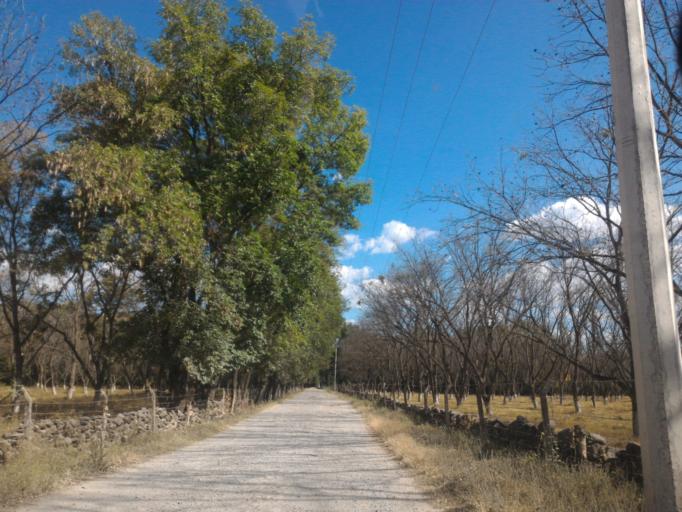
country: MX
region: Jalisco
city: San Diego de Alejandria
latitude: 20.8837
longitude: -101.9892
